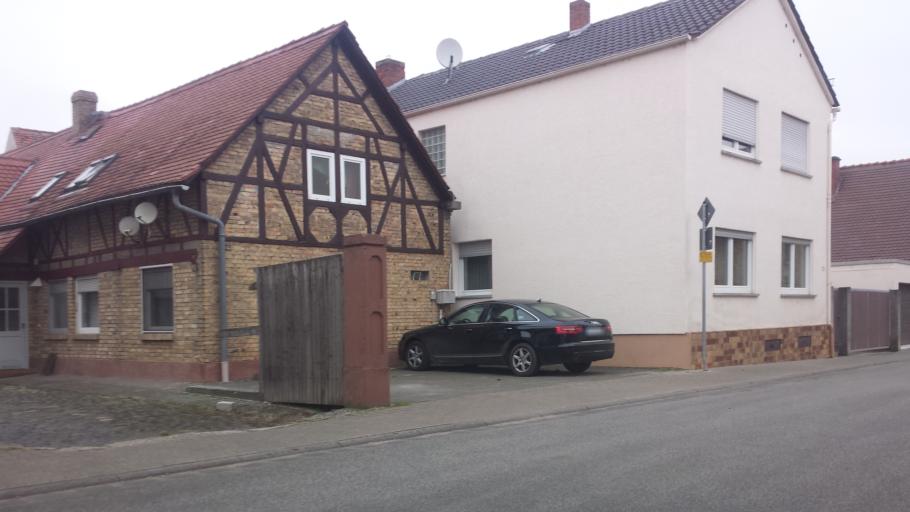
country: DE
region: Rheinland-Pfalz
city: Worms
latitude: 49.6811
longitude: 8.3862
